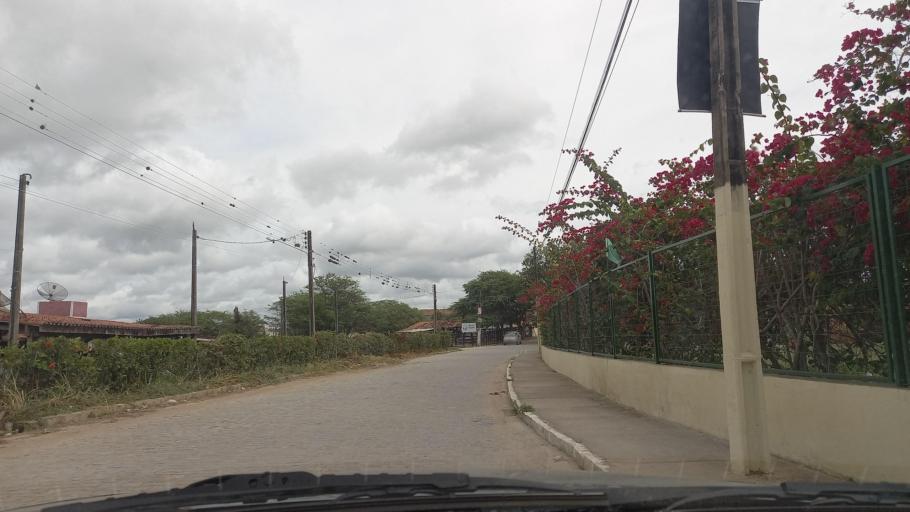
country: ET
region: Oromiya
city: Gore
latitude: 8.1937
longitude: 35.5763
